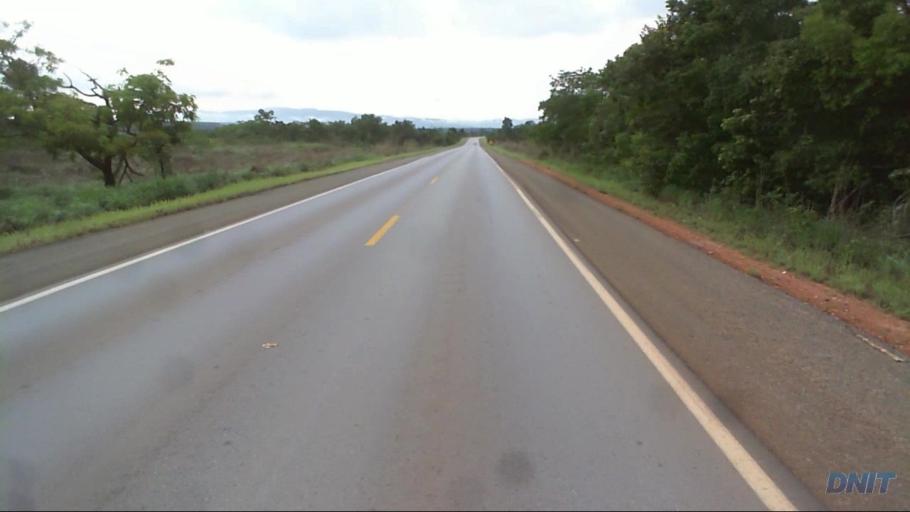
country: BR
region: Goias
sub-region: Uruacu
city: Uruacu
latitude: -14.7336
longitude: -49.0888
